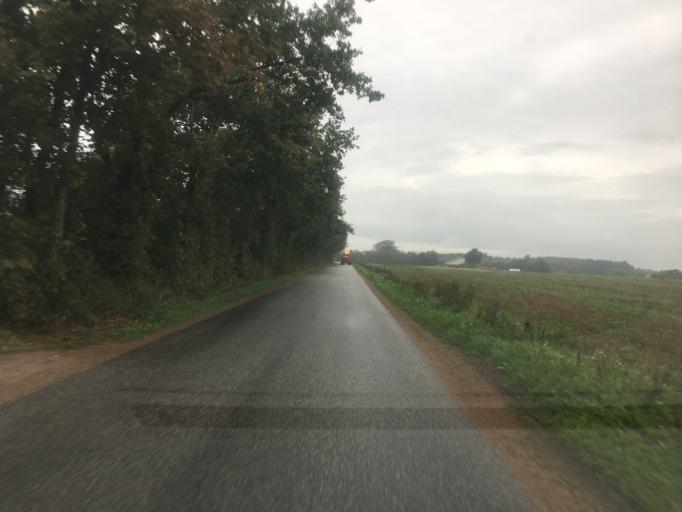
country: DK
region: South Denmark
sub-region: Tonder Kommune
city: Logumkloster
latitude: 55.0232
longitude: 9.0347
